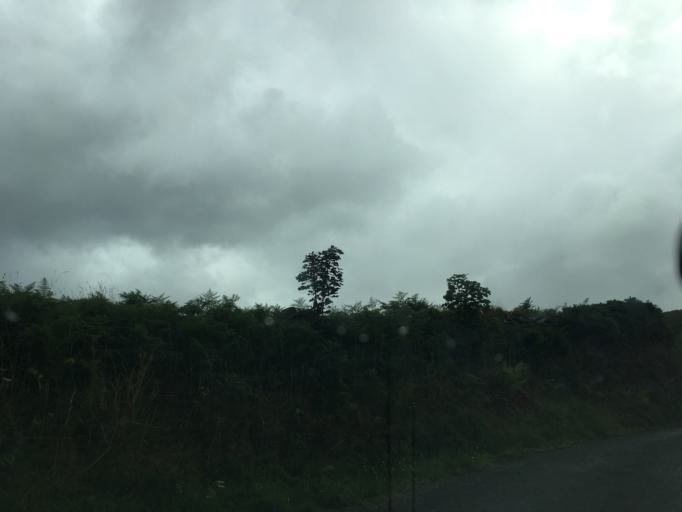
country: GB
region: Scotland
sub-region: Argyll and Bute
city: Oban
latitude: 56.2611
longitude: -5.4703
